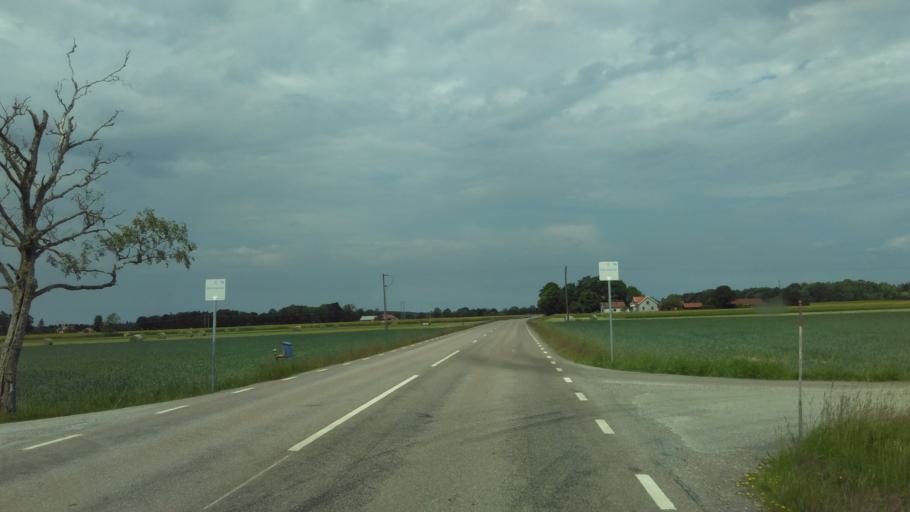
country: SE
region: Vaestra Goetaland
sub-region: Lidkopings Kommun
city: Lidkoping
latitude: 58.4682
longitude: 13.1437
